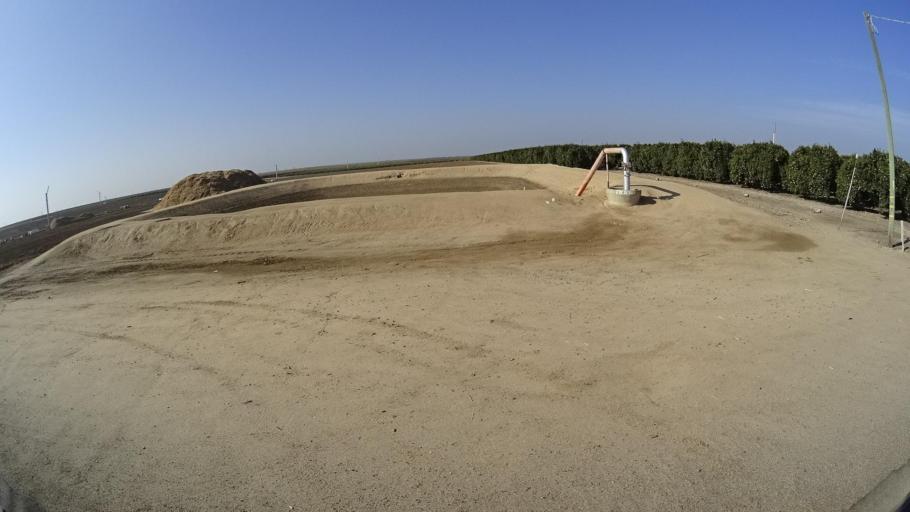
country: US
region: California
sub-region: Kern County
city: McFarland
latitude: 35.6367
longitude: -119.1689
